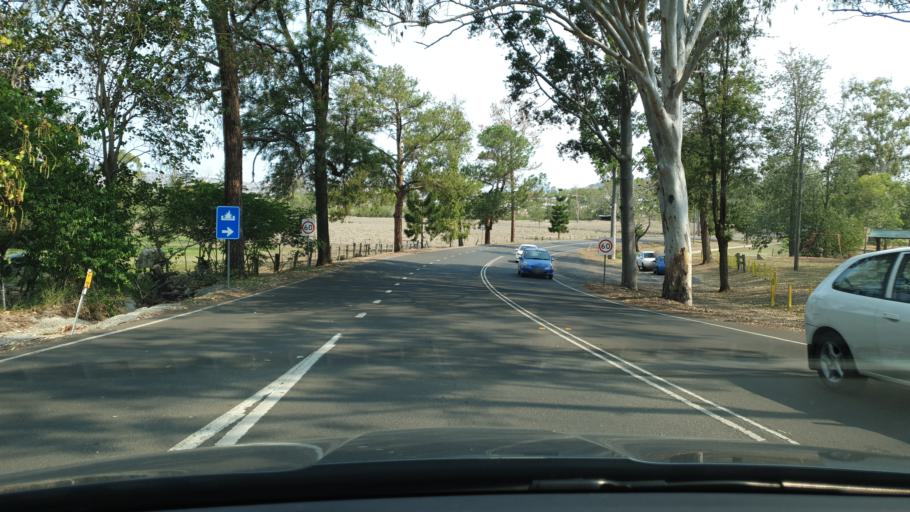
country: AU
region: Queensland
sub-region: Ipswich
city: Deebing Heights
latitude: -28.0000
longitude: 152.6817
